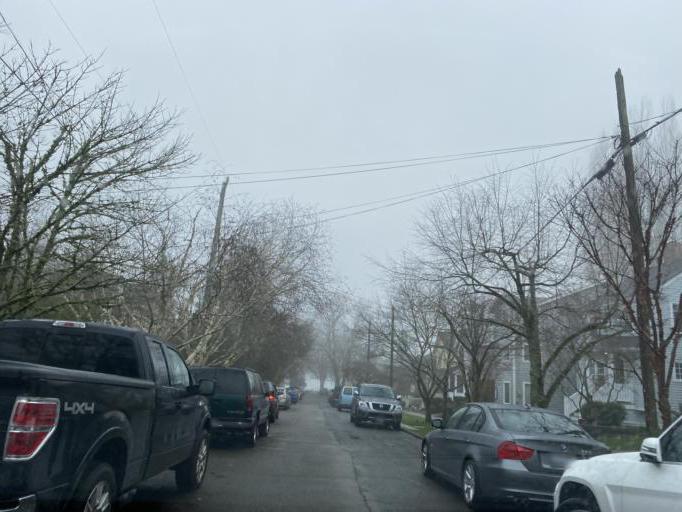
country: US
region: Washington
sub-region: King County
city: Seattle
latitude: 47.6077
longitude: -122.2884
